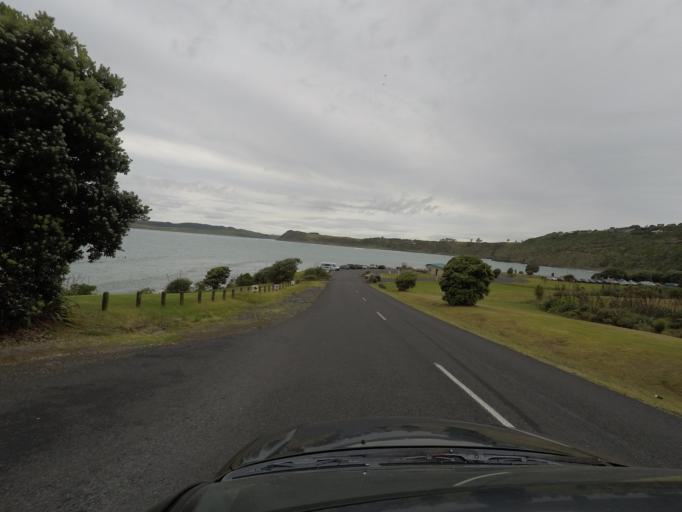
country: NZ
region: Waikato
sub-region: Waikato District
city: Raglan
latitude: -37.8218
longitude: 174.8113
